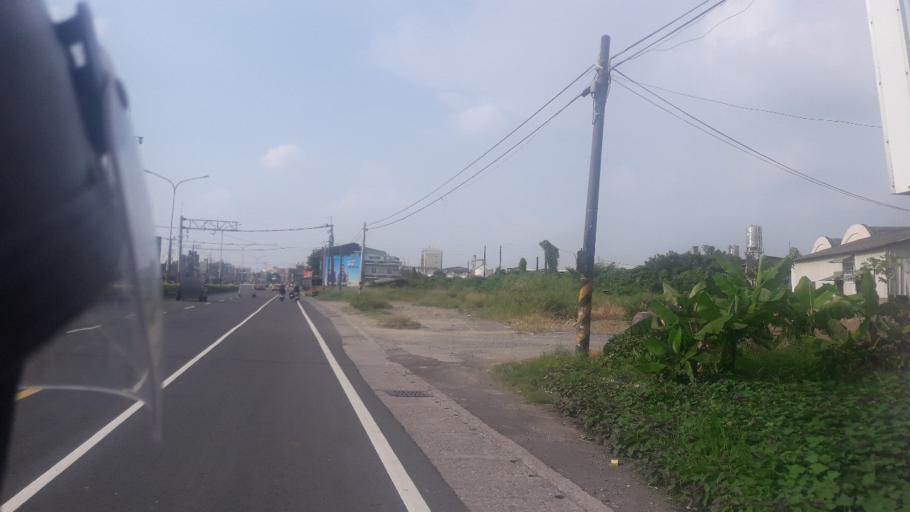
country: TW
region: Taiwan
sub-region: Tainan
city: Tainan
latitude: 22.8739
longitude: 120.2540
